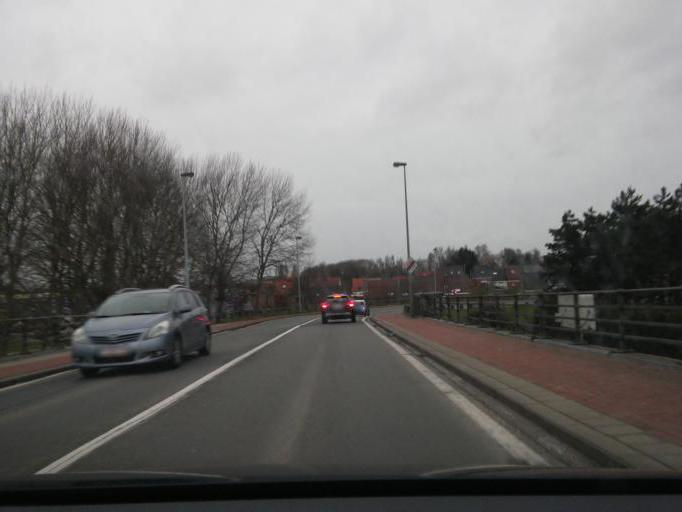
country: BE
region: Flanders
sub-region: Provincie Oost-Vlaanderen
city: Wetteren
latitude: 51.0073
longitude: 3.8764
